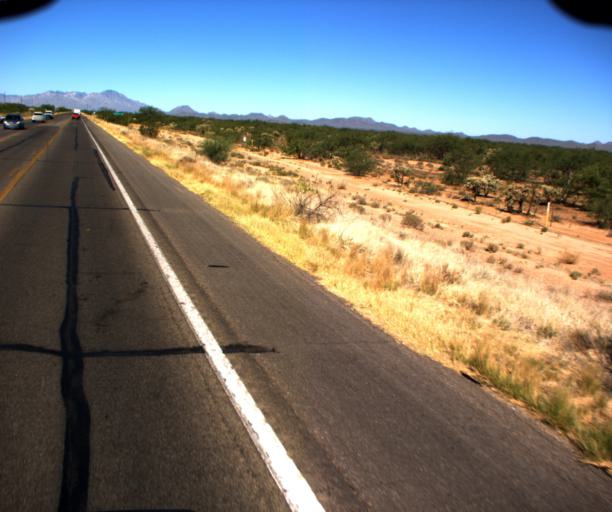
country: US
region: Arizona
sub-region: Pima County
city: Three Points
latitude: 32.1120
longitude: -111.2251
